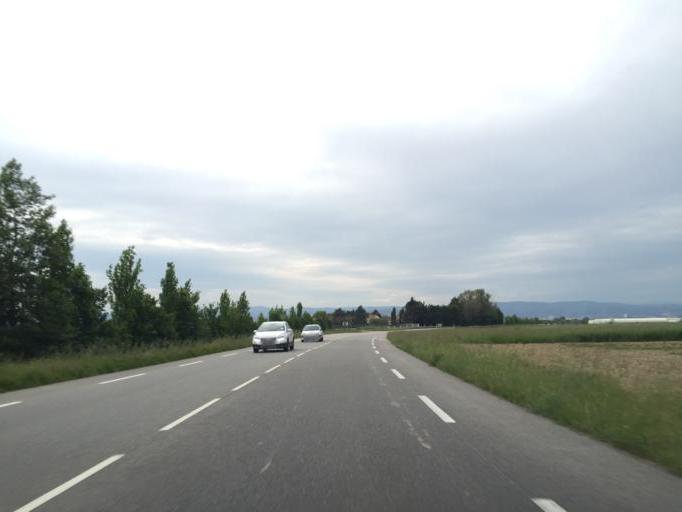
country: FR
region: Rhone-Alpes
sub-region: Departement de la Drome
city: Chabeuil
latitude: 44.9040
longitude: 4.9945
